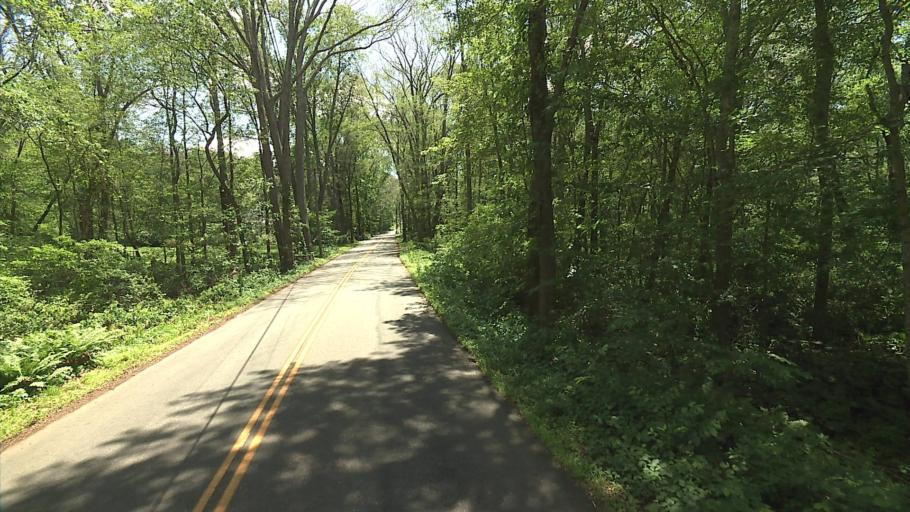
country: US
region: Connecticut
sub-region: New London County
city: Jewett City
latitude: 41.6006
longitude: -71.9062
